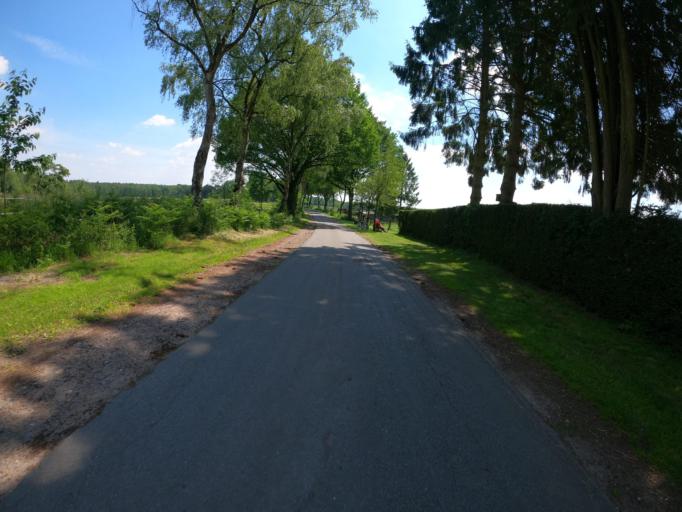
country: DE
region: North Rhine-Westphalia
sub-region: Regierungsbezirk Dusseldorf
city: Hunxe
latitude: 51.7022
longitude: 6.7910
